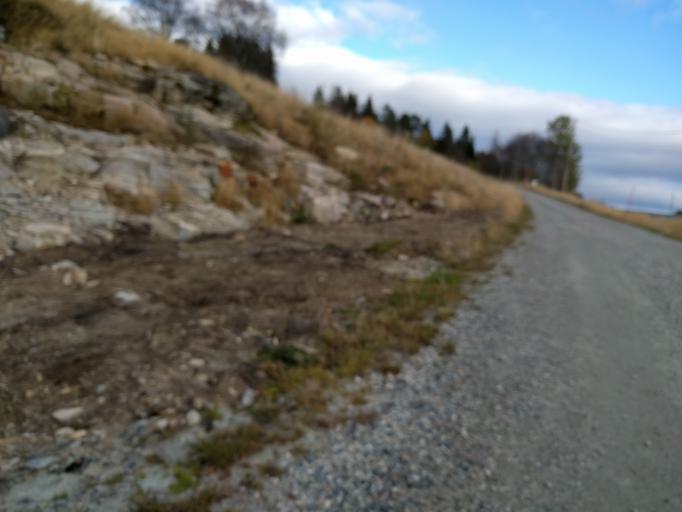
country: NO
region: Aust-Agder
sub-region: Evje og Hornnes
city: Evje
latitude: 58.6511
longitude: 7.9507
